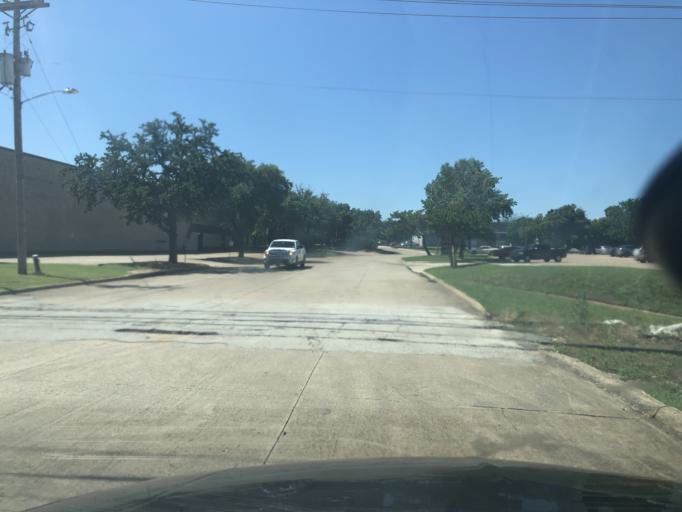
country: US
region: Texas
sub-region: Dallas County
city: Grand Prairie
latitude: 32.7840
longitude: -97.0382
